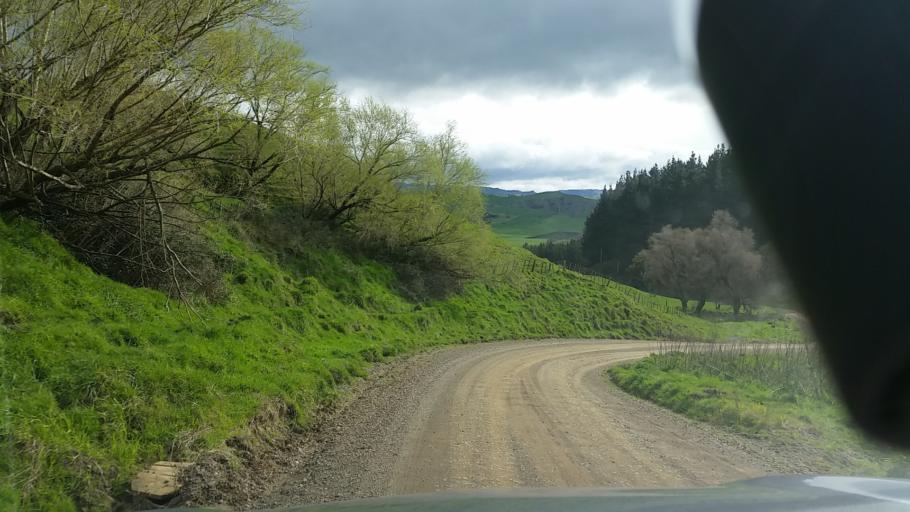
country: NZ
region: Hawke's Bay
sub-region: Napier City
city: Napier
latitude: -39.1926
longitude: 176.9165
